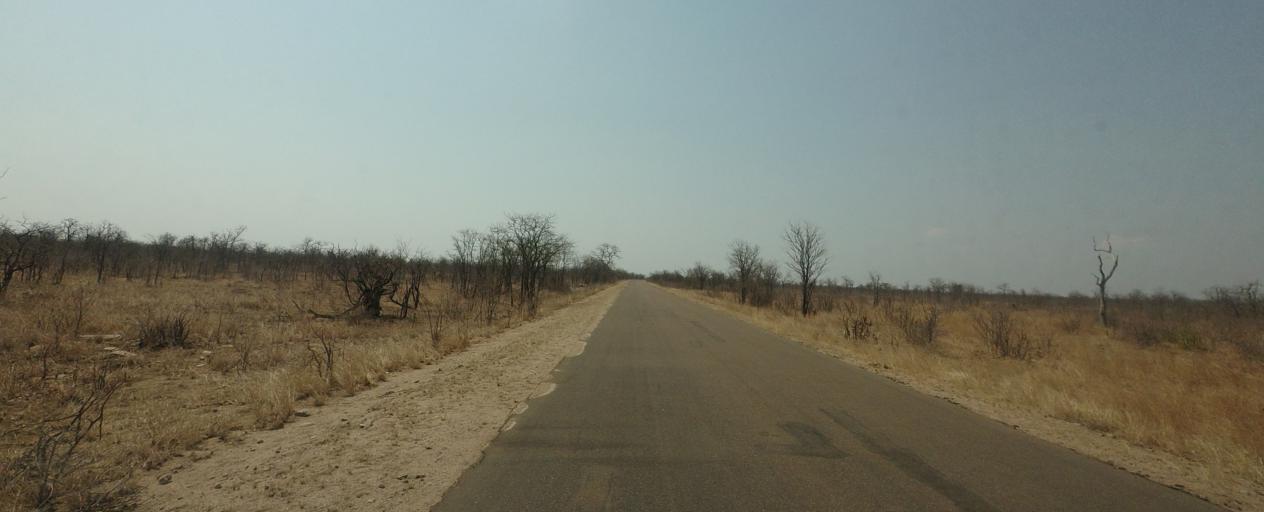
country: ZA
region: Limpopo
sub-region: Mopani District Municipality
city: Giyani
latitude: -23.3566
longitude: 31.3190
